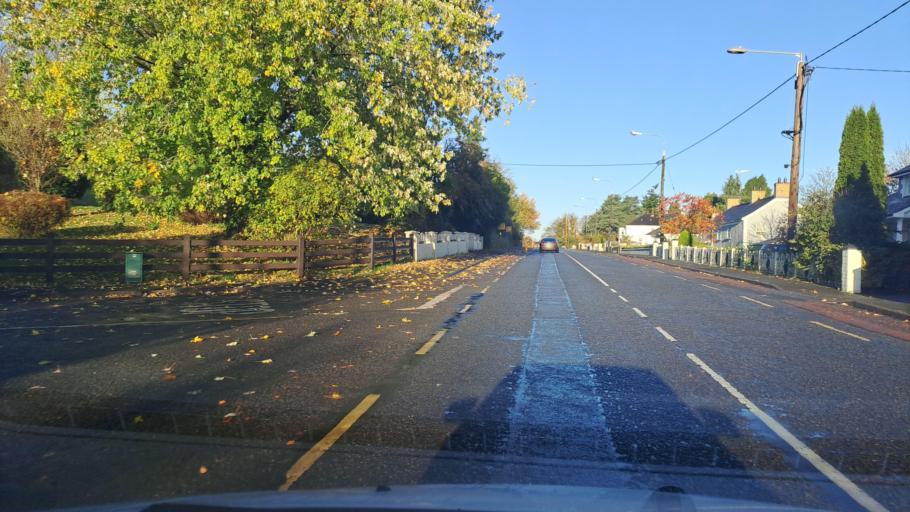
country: IE
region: Ulster
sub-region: An Cabhan
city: Cootehill
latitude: 54.0721
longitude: -7.0718
